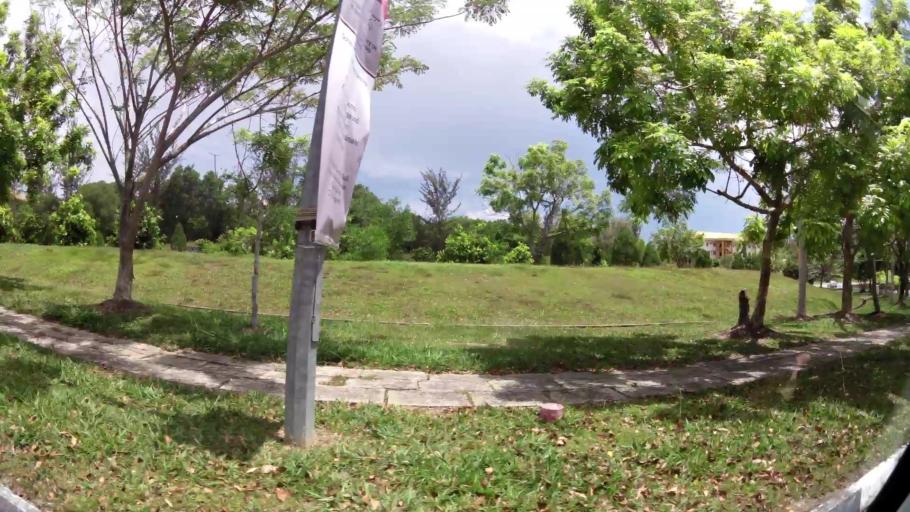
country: BN
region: Brunei and Muara
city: Bandar Seri Begawan
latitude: 4.9733
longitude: 114.8917
